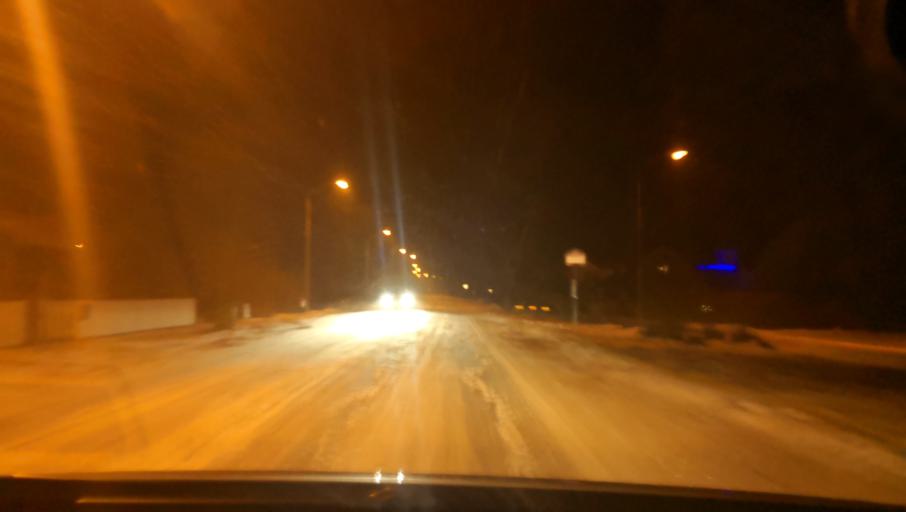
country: SE
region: Uppsala
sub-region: Heby Kommun
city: Tarnsjo
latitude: 60.1508
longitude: 16.9225
